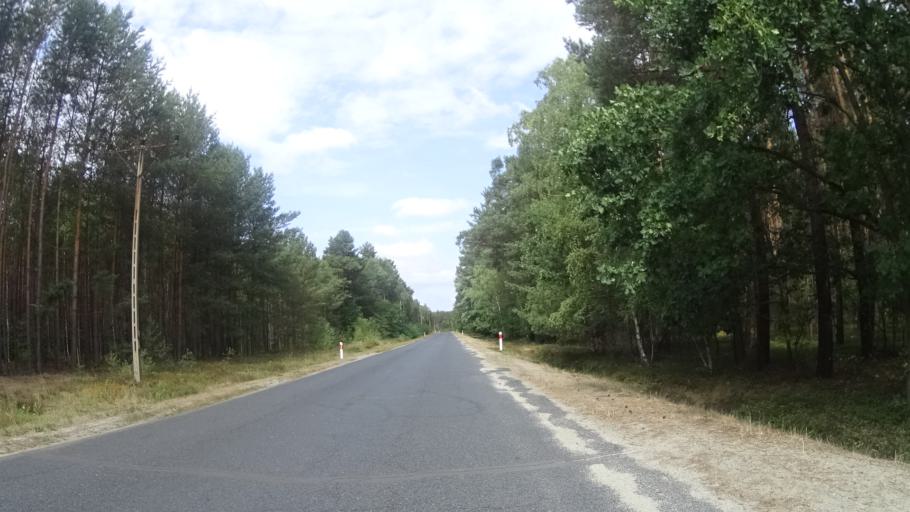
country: PL
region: Lubusz
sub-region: Powiat zarski
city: Leknica
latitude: 51.5316
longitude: 14.8132
